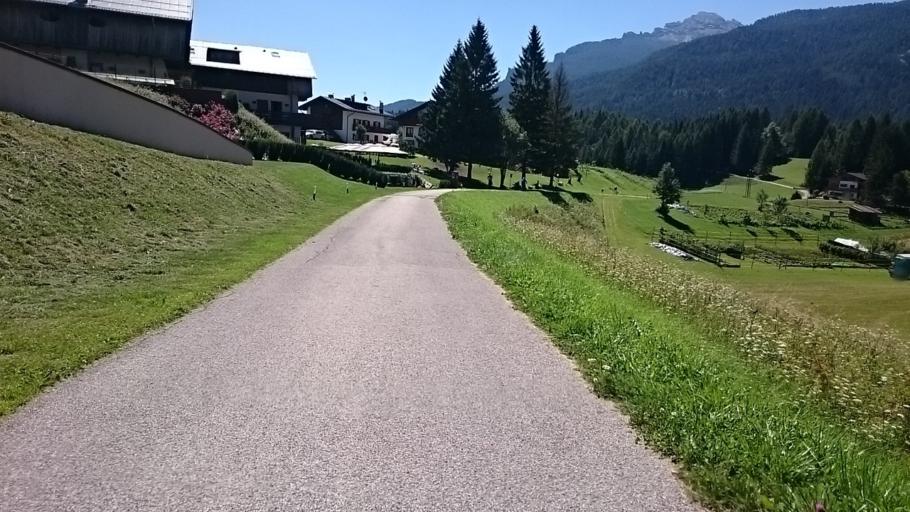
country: IT
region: Veneto
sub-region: Provincia di Belluno
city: Cortina d'Ampezzo
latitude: 46.5168
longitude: 12.1423
